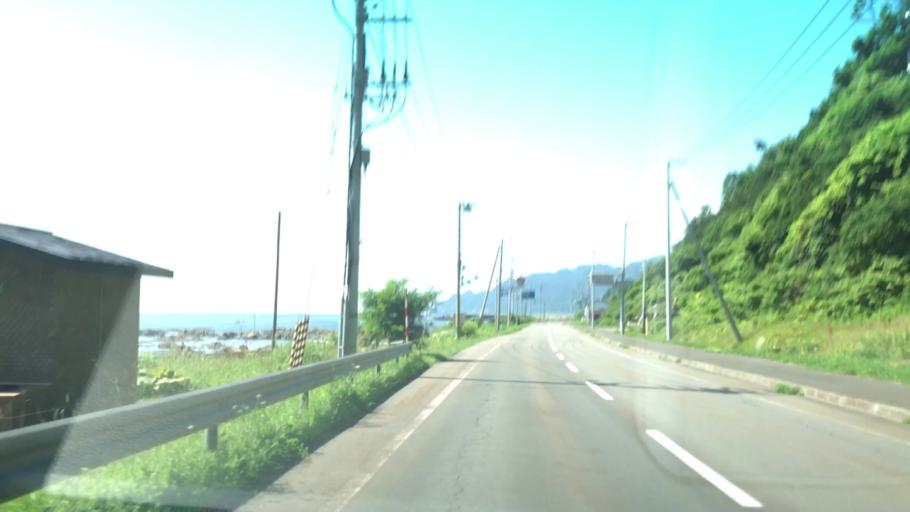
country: JP
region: Hokkaido
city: Iwanai
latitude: 43.0892
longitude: 140.4654
